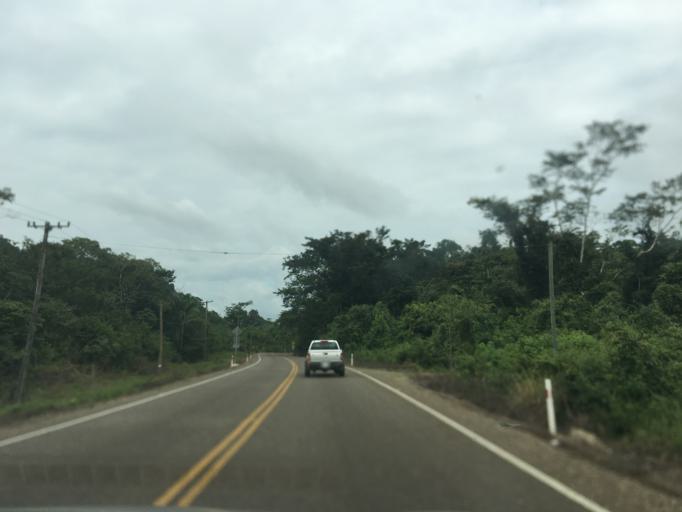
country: BZ
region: Cayo
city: Belmopan
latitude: 17.1960
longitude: -88.7728
